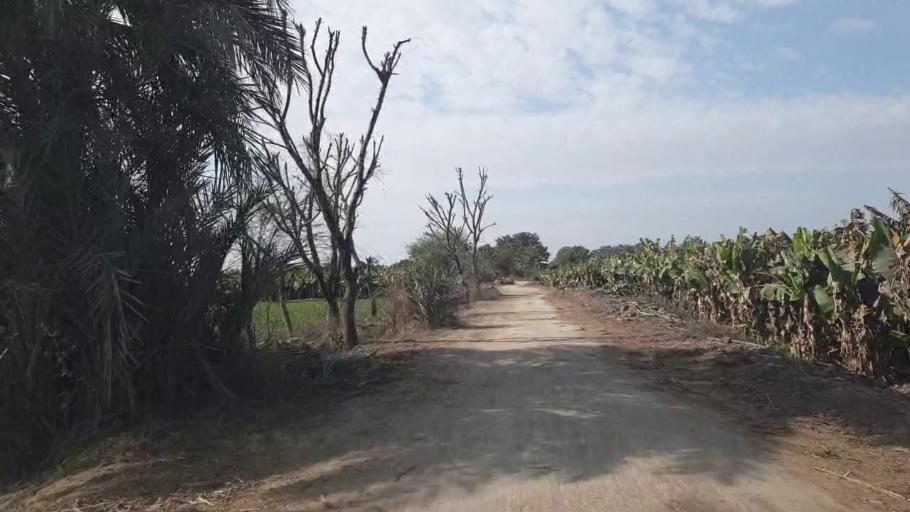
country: PK
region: Sindh
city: Sakrand
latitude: 25.9893
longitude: 68.3368
